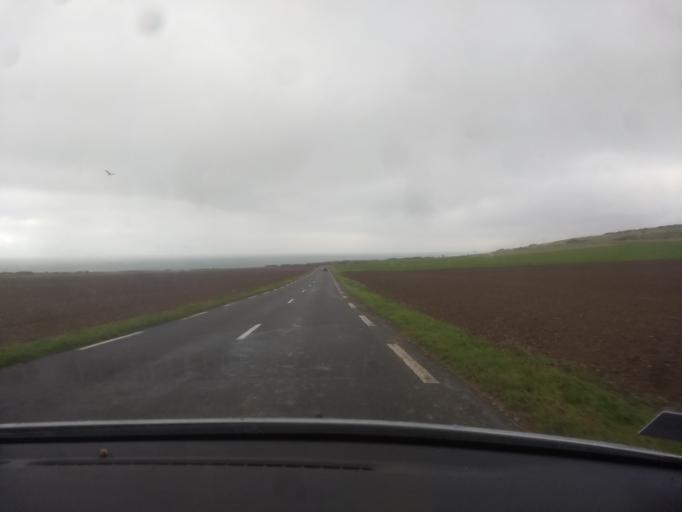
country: FR
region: Nord-Pas-de-Calais
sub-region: Departement du Pas-de-Calais
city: Sangatte
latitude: 50.9333
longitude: 1.7236
